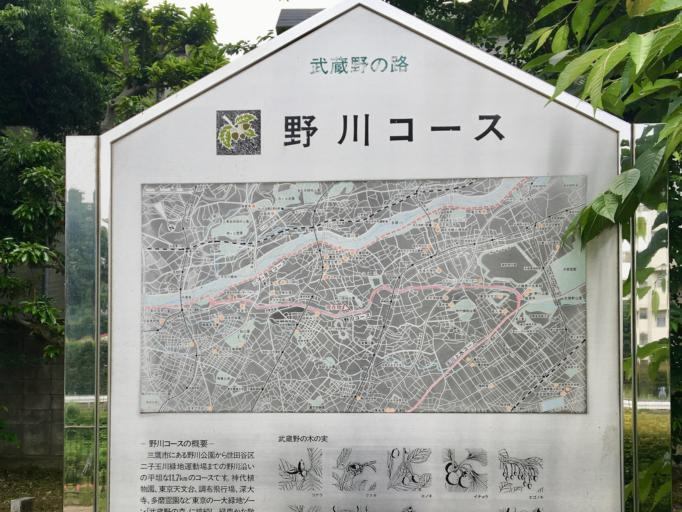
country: JP
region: Tokyo
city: Chofugaoka
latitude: 35.6507
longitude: 139.5751
